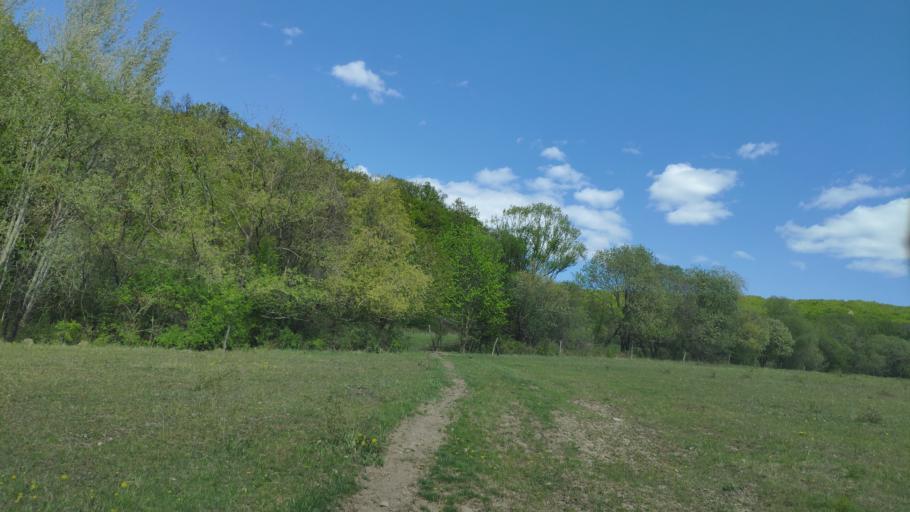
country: SK
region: Kosicky
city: Kosice
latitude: 48.6544
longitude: 21.4340
